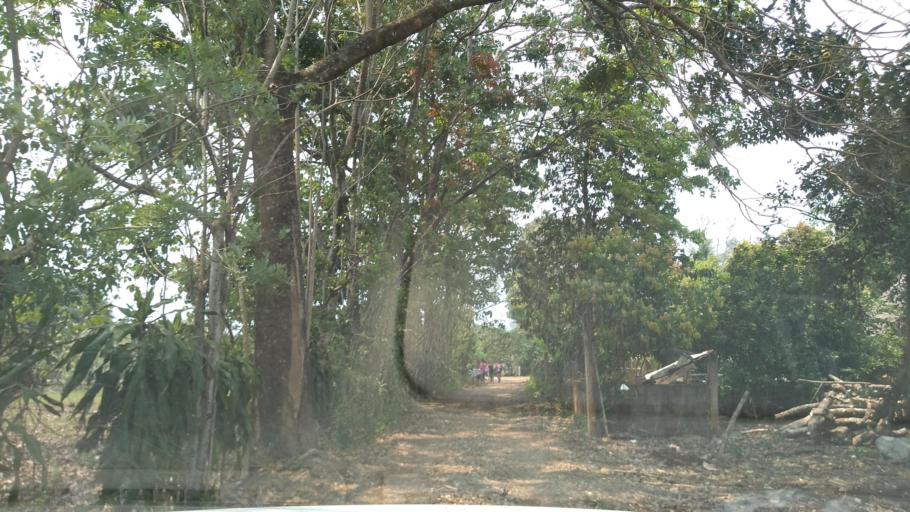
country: MX
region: Veracruz
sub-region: Tezonapa
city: Laguna Chica (Pueblo Nuevo)
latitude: 18.5296
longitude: -96.7624
